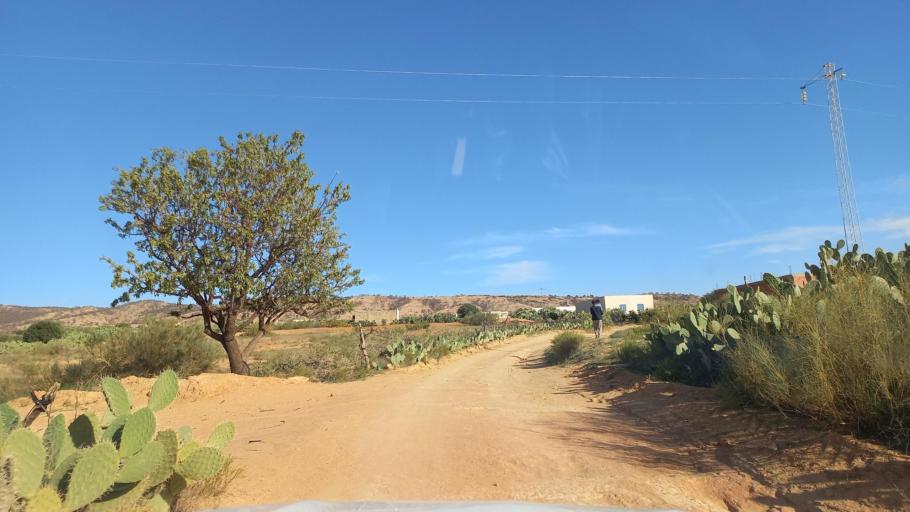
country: TN
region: Al Qasrayn
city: Sbiba
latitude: 35.3295
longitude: 9.1278
